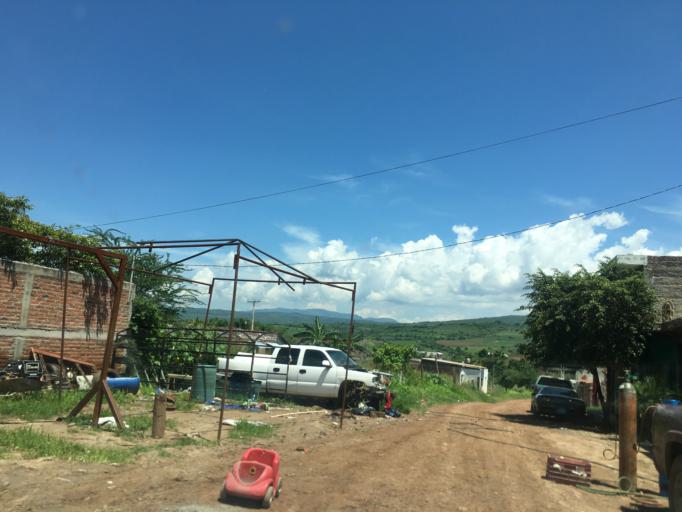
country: MX
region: Nayarit
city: Ixtlan del Rio
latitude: 21.0366
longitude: -104.3543
